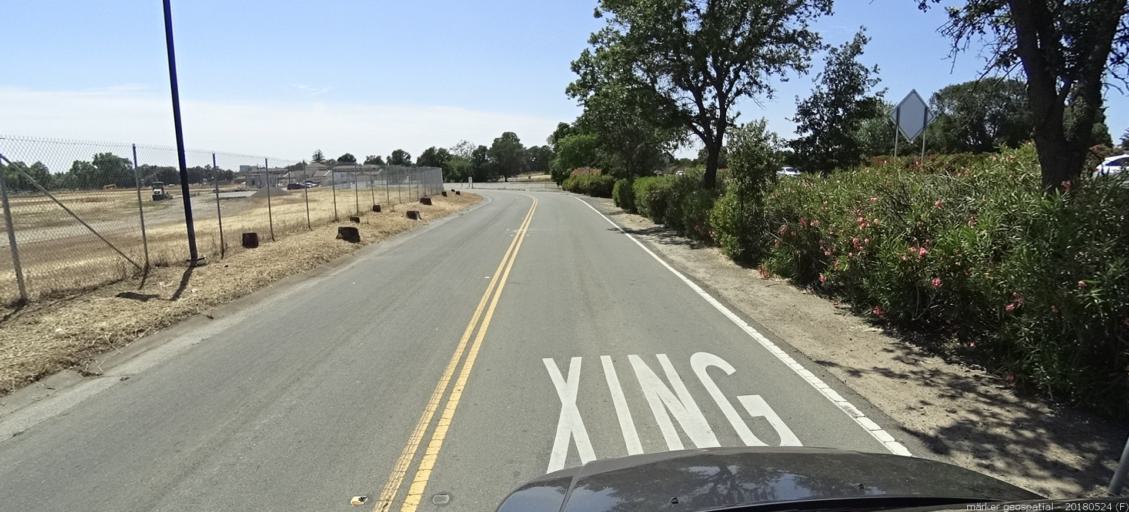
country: US
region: California
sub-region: Sacramento County
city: Sacramento
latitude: 38.5998
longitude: -121.4534
